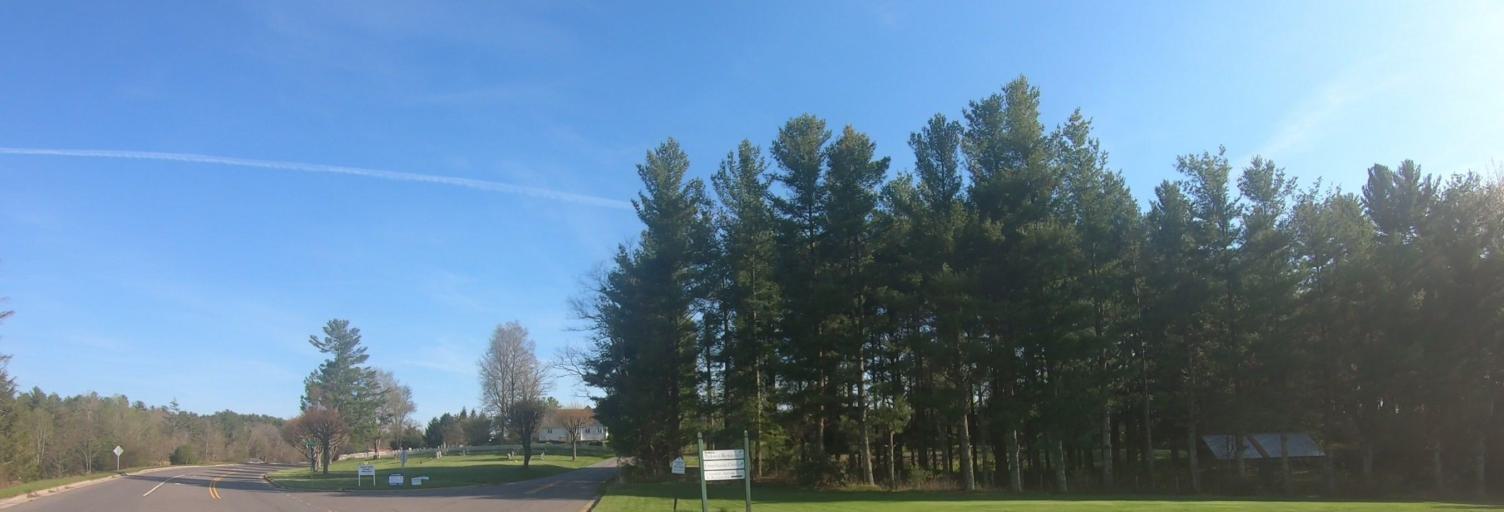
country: US
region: North Carolina
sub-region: Ashe County
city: Jefferson
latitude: 36.3485
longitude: -81.3809
